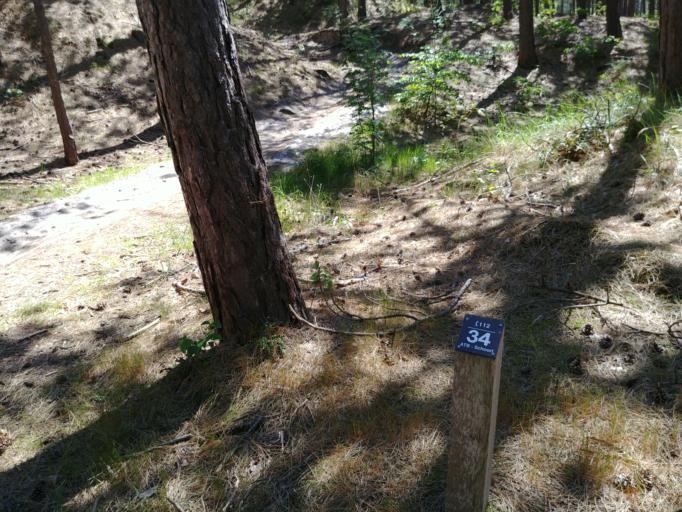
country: NL
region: North Holland
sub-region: Gemeente Bergen
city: Egmond aan Zee
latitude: 52.6785
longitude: 4.6448
